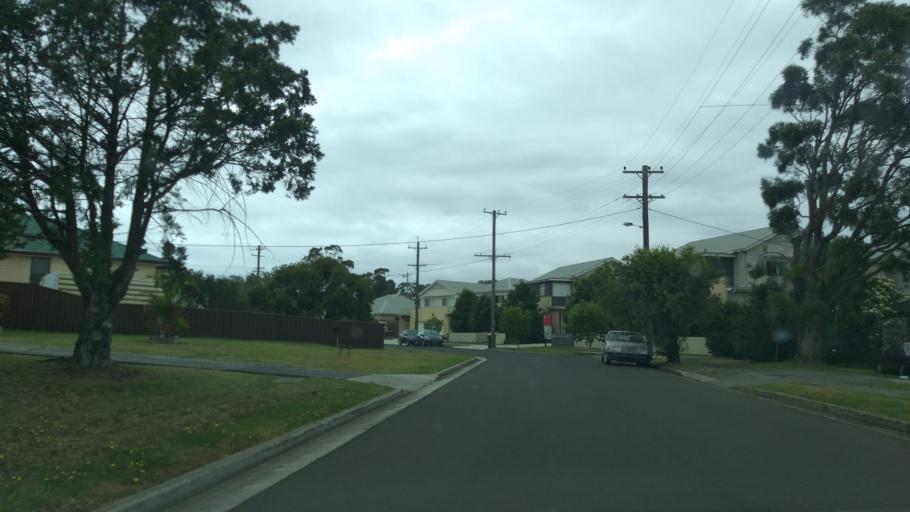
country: AU
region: New South Wales
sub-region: Wollongong
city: Berkeley
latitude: -34.4826
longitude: 150.8405
